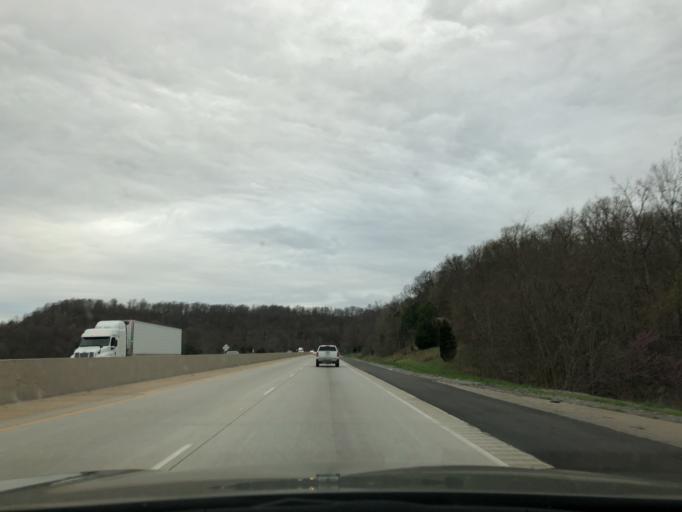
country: US
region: Arkansas
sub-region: Washington County
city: West Fork
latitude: 35.7779
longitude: -94.1864
